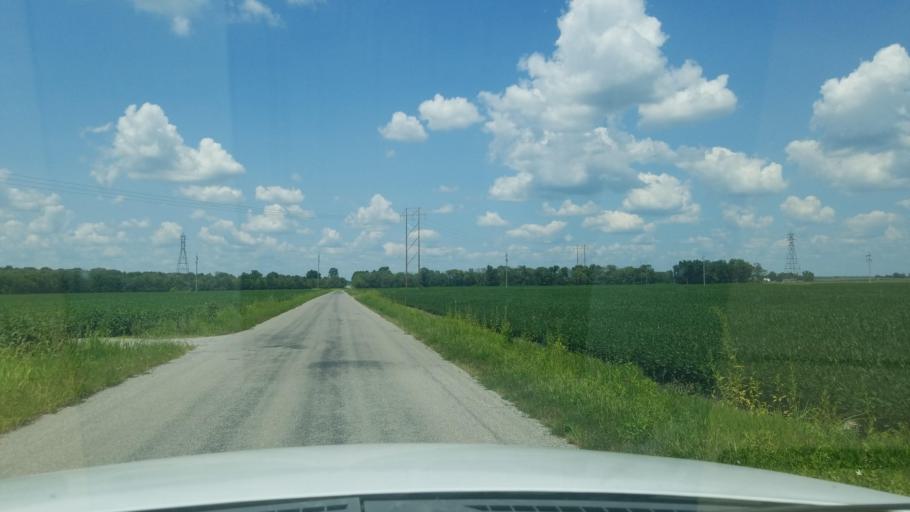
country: US
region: Illinois
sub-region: Saline County
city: Harrisburg
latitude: 37.7729
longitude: -88.5171
